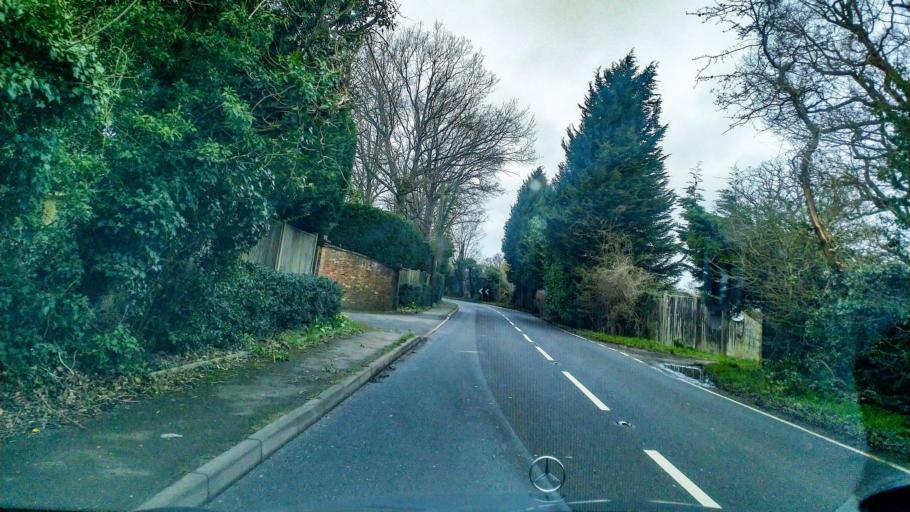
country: GB
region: England
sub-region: Surrey
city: Reigate
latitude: 51.2104
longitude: -0.2540
